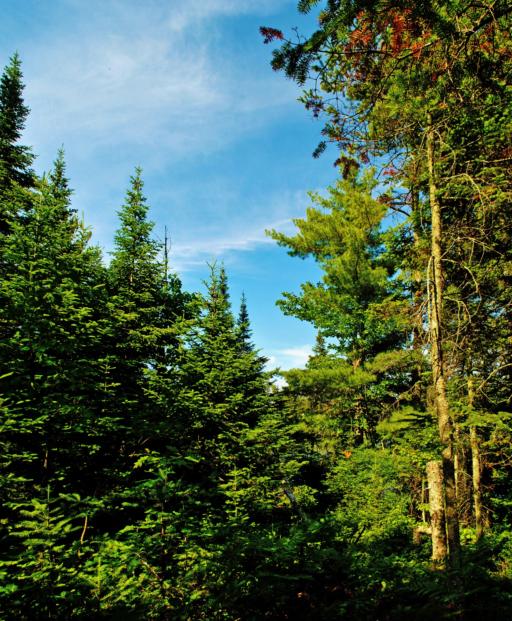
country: US
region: Wisconsin
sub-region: Sawyer County
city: Little Round Lake
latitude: 46.1239
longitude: -91.2427
